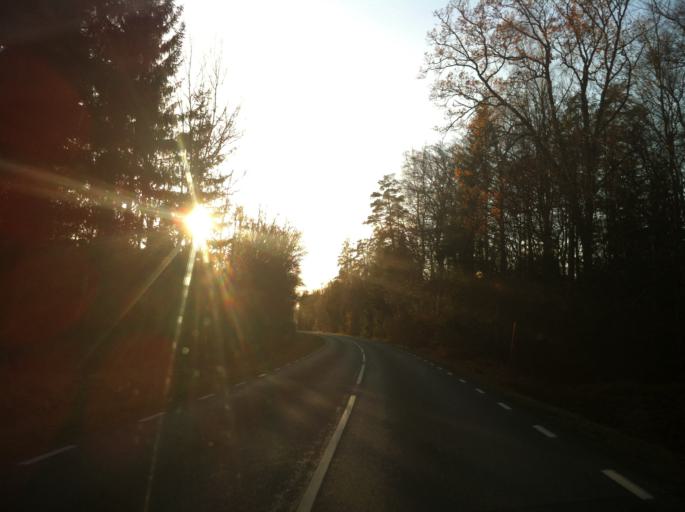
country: SE
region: Skane
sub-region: Ostra Goinge Kommun
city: Knislinge
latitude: 56.1865
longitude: 14.0605
